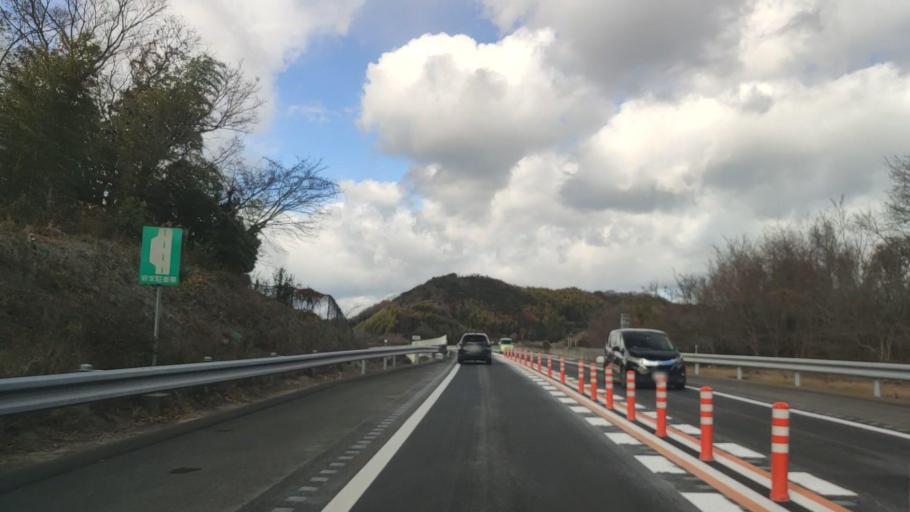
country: JP
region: Hiroshima
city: Innoshima
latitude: 34.3116
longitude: 133.1557
